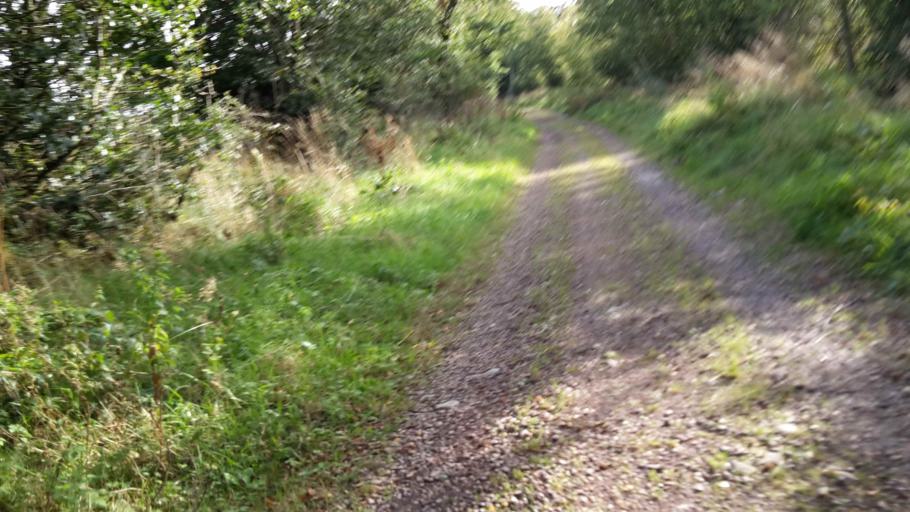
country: GB
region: Scotland
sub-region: South Lanarkshire
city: Carluke
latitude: 55.7221
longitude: -3.8280
